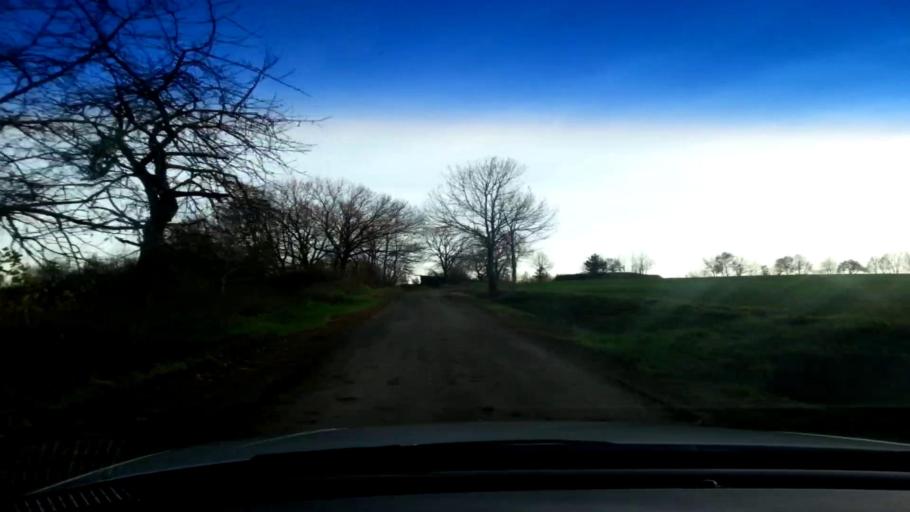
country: DE
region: Bavaria
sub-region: Upper Franconia
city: Ebensfeld
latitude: 50.0390
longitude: 10.9555
